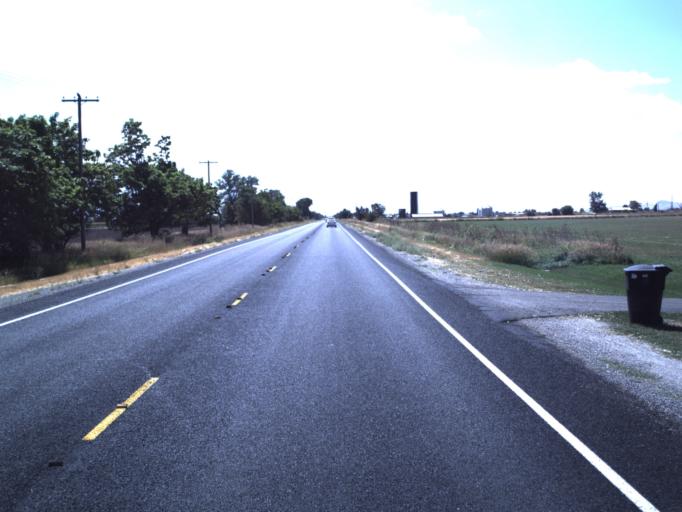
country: US
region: Utah
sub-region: Box Elder County
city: Garland
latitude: 41.7780
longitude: -112.1492
